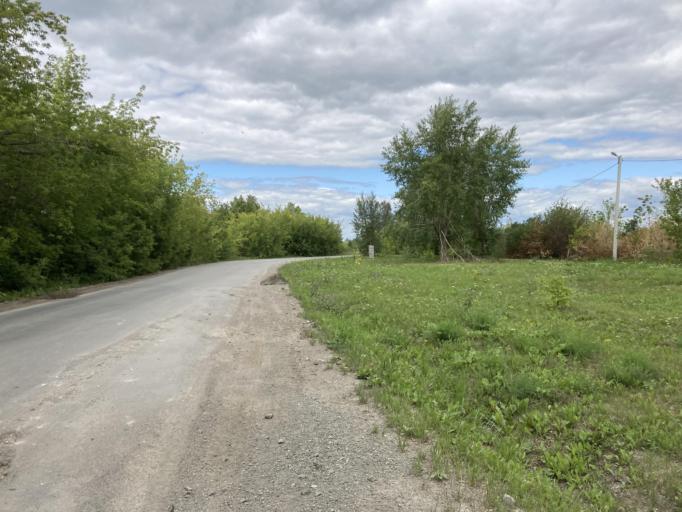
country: RU
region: Sverdlovsk
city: Bogdanovich
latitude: 56.7858
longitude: 62.0661
